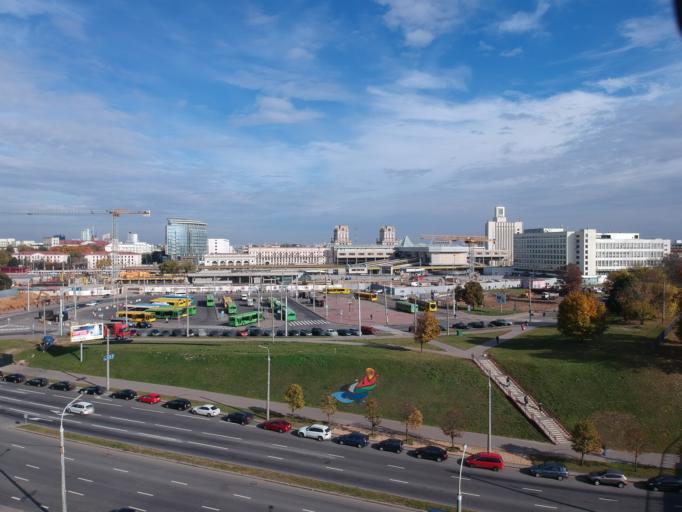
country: BY
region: Minsk
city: Minsk
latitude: 53.8872
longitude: 27.5458
